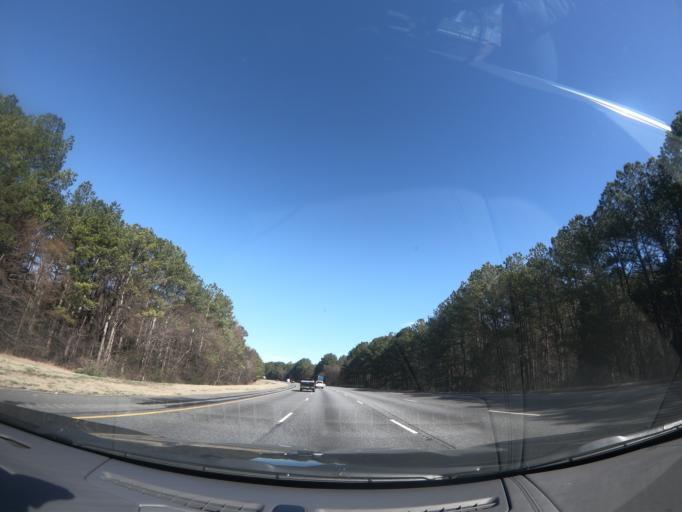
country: US
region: Georgia
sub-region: Bartow County
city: Adairsville
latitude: 34.4142
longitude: -84.9179
